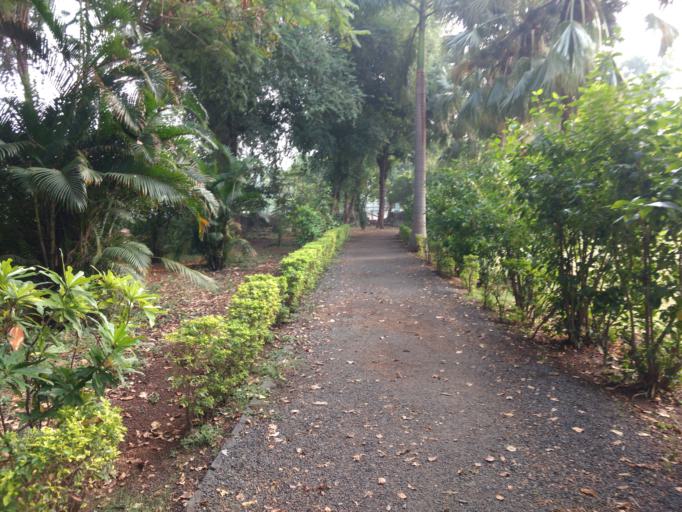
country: IN
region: Maharashtra
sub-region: Nagpur Division
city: Nagpur
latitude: 21.1550
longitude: 79.0509
